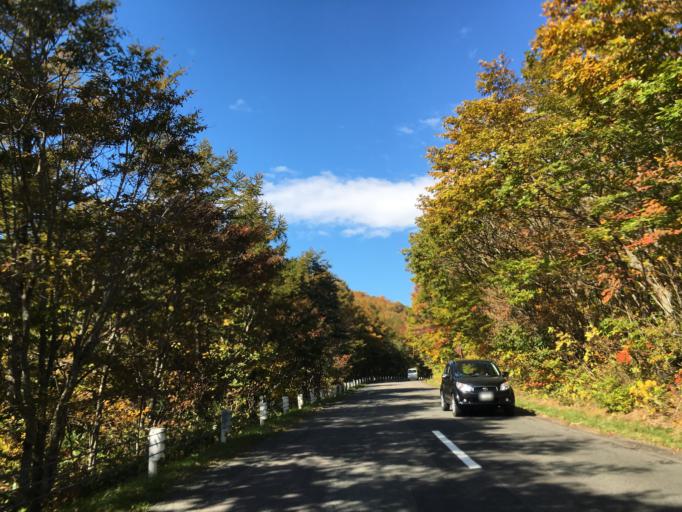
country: JP
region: Fukushima
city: Inawashiro
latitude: 37.5855
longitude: 140.2441
